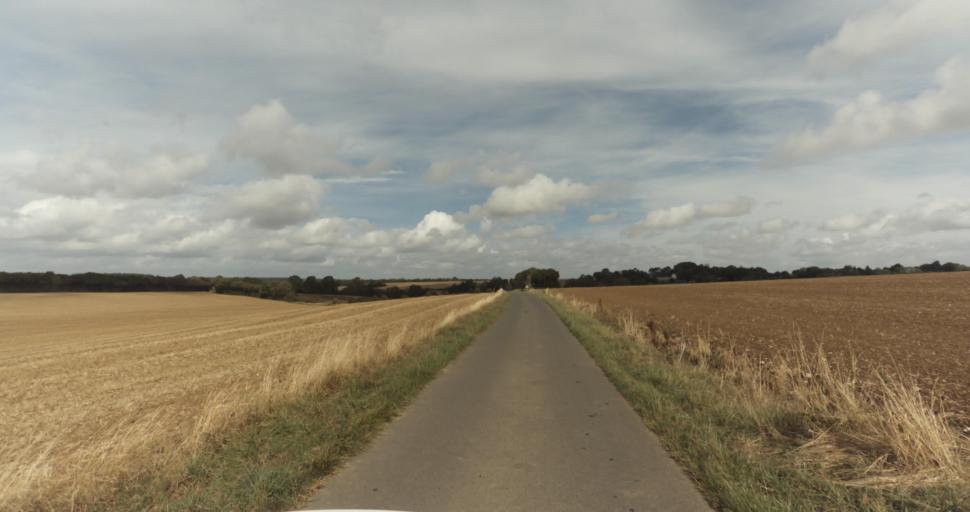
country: FR
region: Lower Normandy
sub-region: Departement de l'Orne
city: Gace
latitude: 48.8061
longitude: 0.3756
